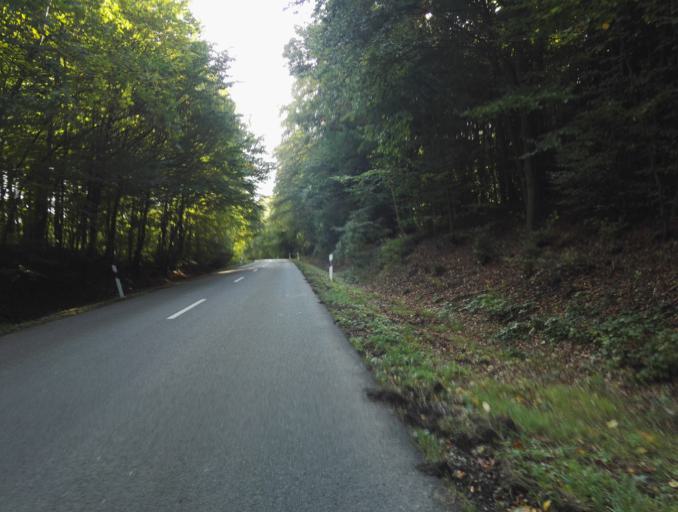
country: DE
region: Lower Saxony
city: Holle
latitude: 52.1347
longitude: 10.1401
